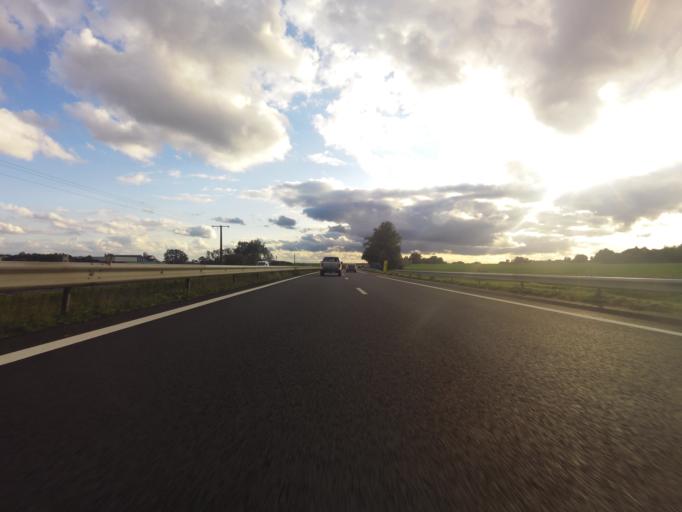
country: FR
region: Haute-Normandie
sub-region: Departement de la Seine-Maritime
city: Blainville-Crevon
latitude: 49.5657
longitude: 1.2729
